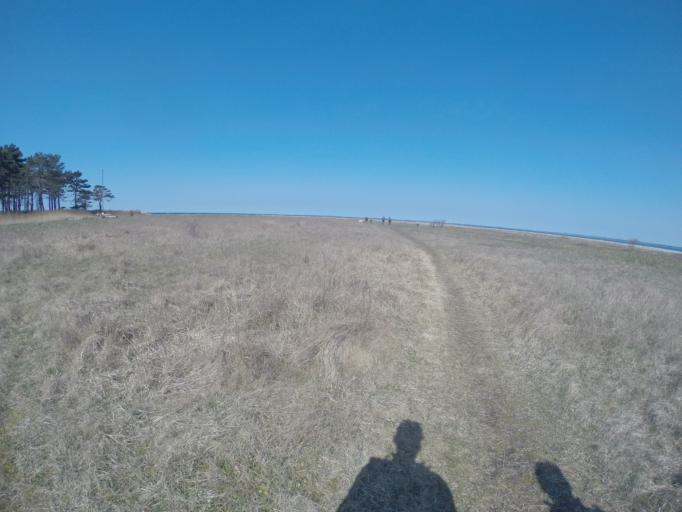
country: DK
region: Zealand
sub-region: Kalundborg Kommune
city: Gorlev
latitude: 55.5349
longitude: 11.0967
